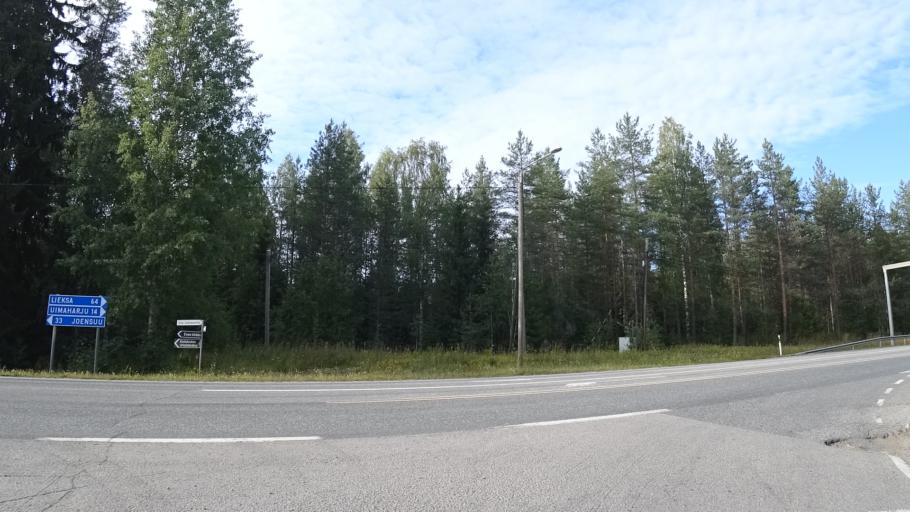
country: FI
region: North Karelia
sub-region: Joensuu
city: Eno
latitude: 62.8083
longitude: 30.1509
